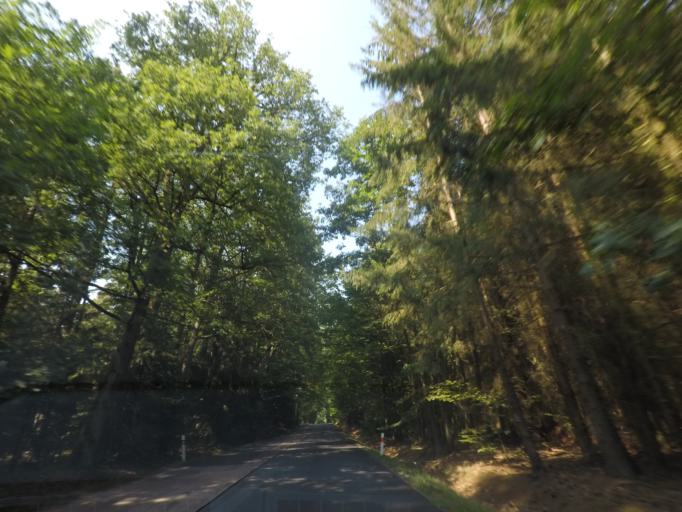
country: CZ
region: Pardubicky
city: Horni Jeleni
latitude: 50.0286
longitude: 16.0818
